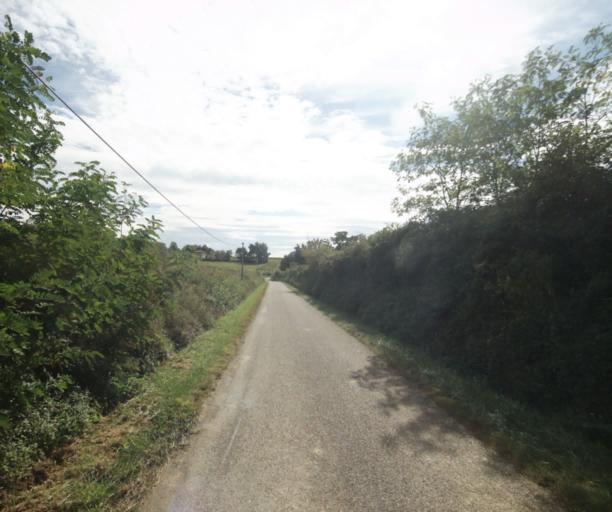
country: FR
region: Aquitaine
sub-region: Departement des Landes
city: Villeneuve-de-Marsan
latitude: 43.8977
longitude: -0.1954
